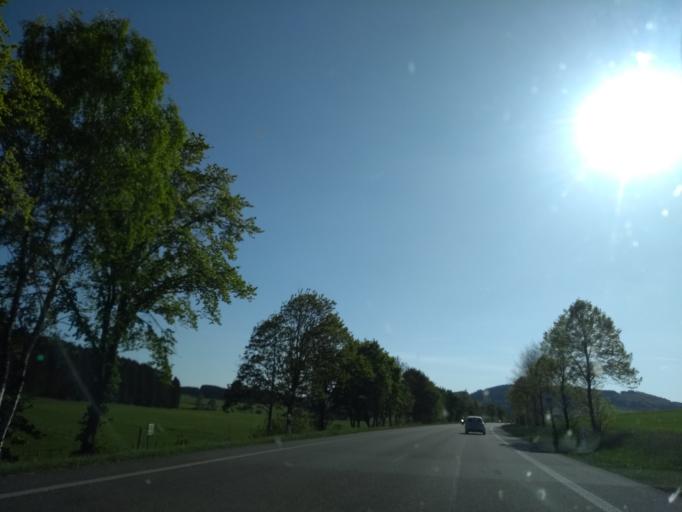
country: DE
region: Hesse
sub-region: Regierungsbezirk Giessen
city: Breidenbach
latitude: 50.8455
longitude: 8.4012
